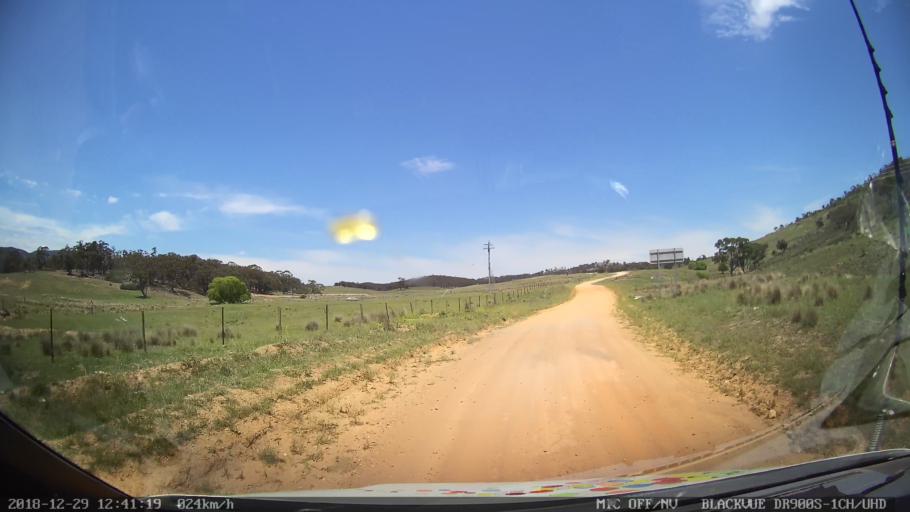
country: AU
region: Australian Capital Territory
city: Macarthur
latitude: -35.6075
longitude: 149.2228
